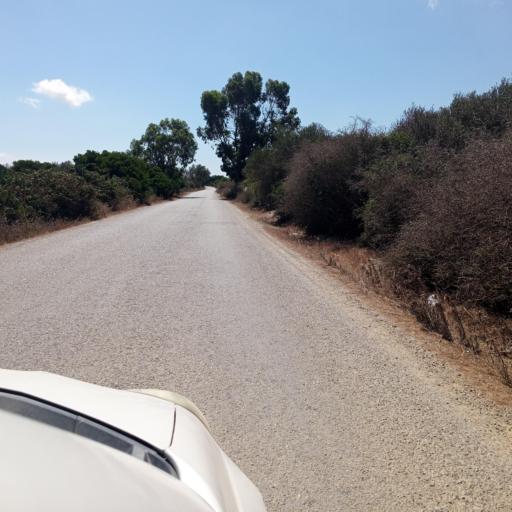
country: TN
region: Nabul
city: Qulaybiyah
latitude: 36.8623
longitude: 11.0396
